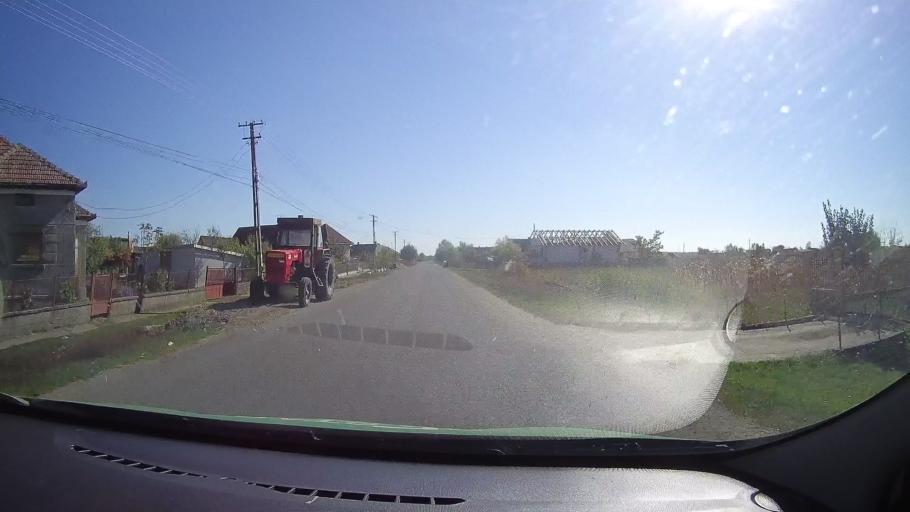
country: RO
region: Satu Mare
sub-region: Comuna Doba
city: Doba
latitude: 47.7420
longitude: 22.7149
